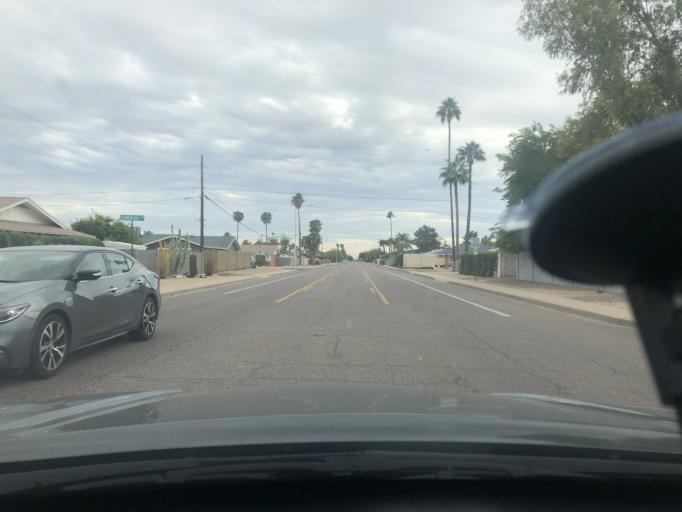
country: US
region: Arizona
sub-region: Maricopa County
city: Scottsdale
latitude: 33.4776
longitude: -111.9004
